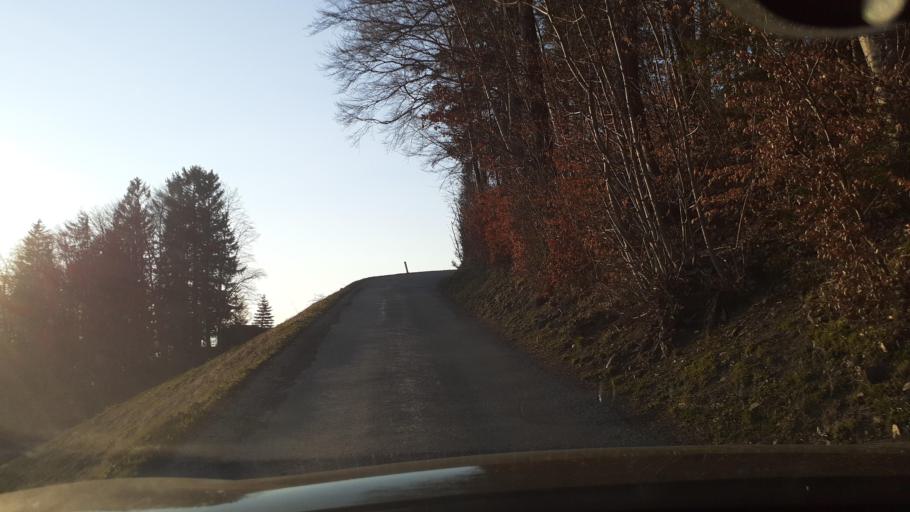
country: AT
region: Vorarlberg
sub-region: Politischer Bezirk Feldkirch
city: Fraxern
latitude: 47.3191
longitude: 9.6776
